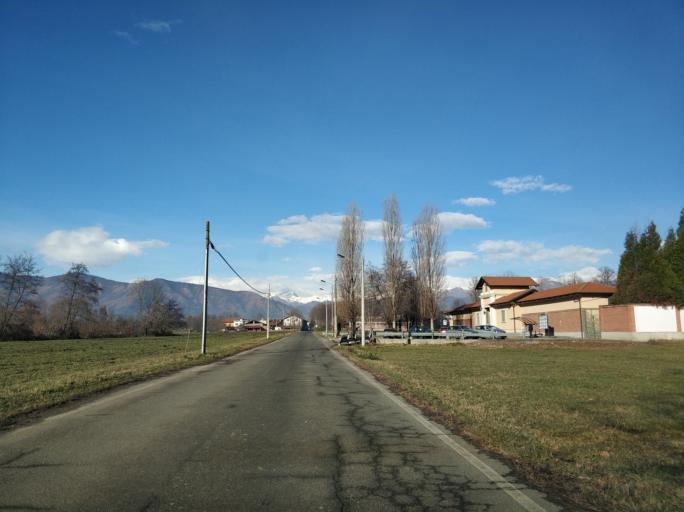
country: IT
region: Piedmont
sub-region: Provincia di Torino
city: Cirie
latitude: 45.2151
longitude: 7.5869
